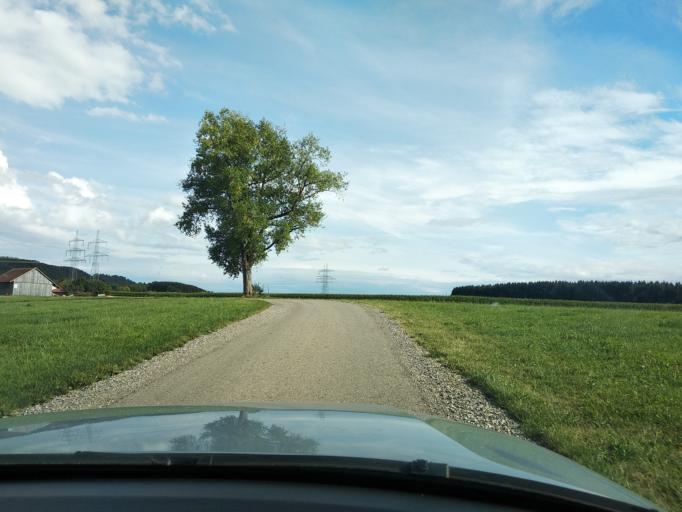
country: DE
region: Bavaria
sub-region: Swabia
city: Wolfertschwenden
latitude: 47.8642
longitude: 10.2619
